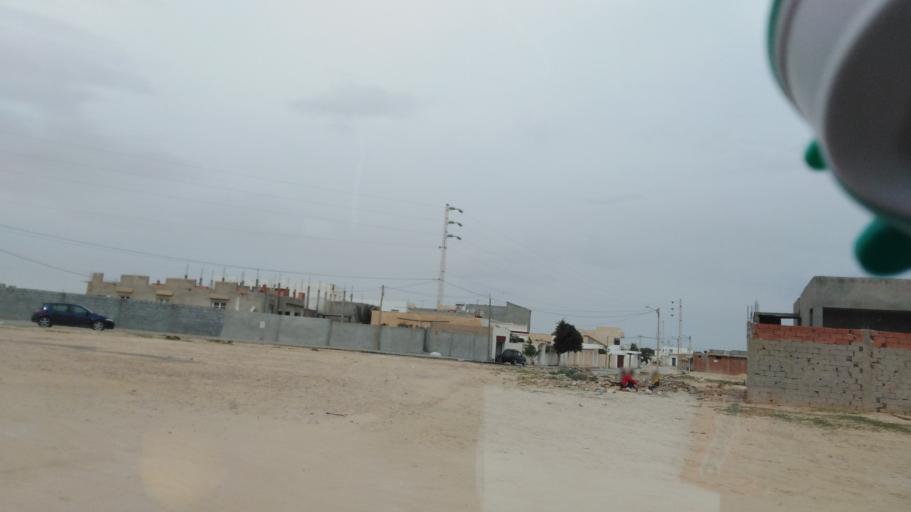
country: TN
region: Qabis
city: Gabes
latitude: 33.9527
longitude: 10.0040
